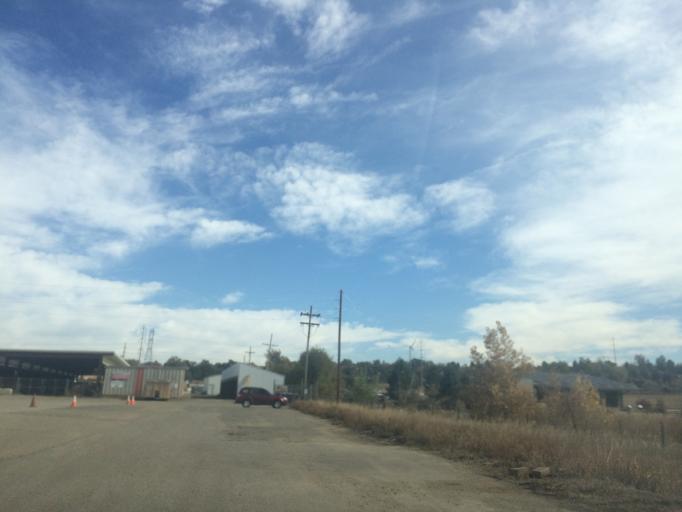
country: US
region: Colorado
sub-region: Boulder County
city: Gunbarrel
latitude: 40.0123
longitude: -105.2034
